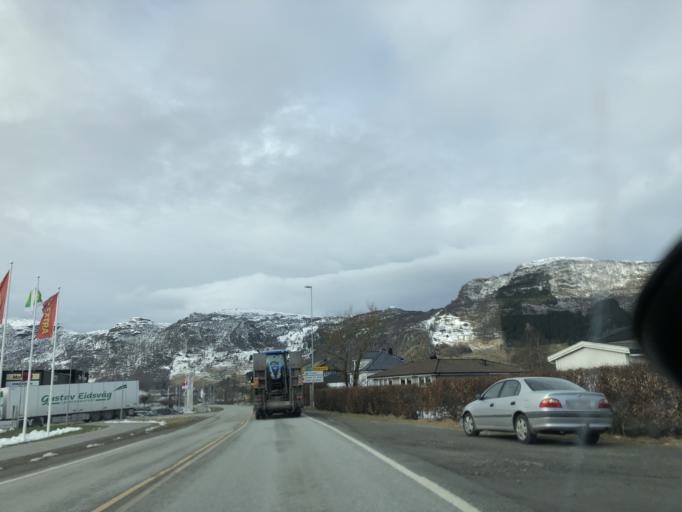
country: NO
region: Hordaland
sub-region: Etne
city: Etne
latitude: 59.6637
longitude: 5.9436
